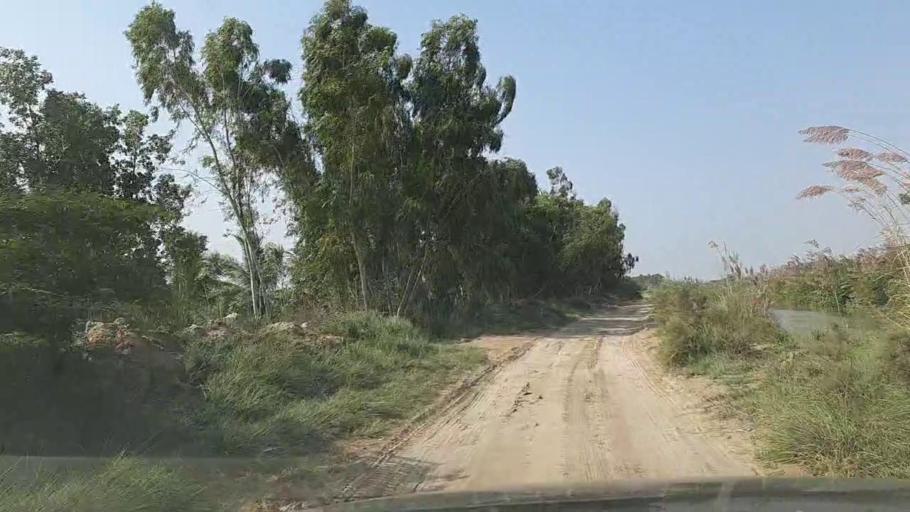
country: PK
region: Sindh
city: Gharo
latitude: 24.7221
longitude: 67.6800
